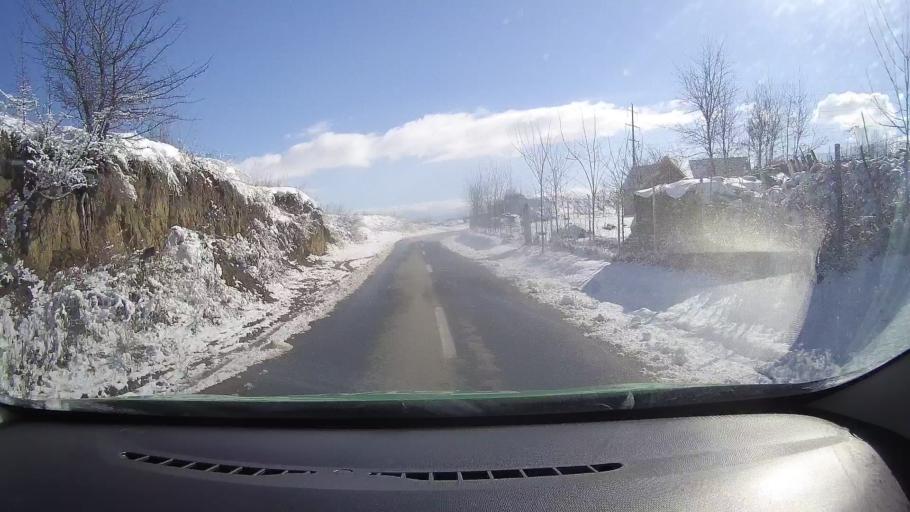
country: RO
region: Sibiu
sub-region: Comuna Rosia
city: Rosia
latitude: 45.7971
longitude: 24.2923
